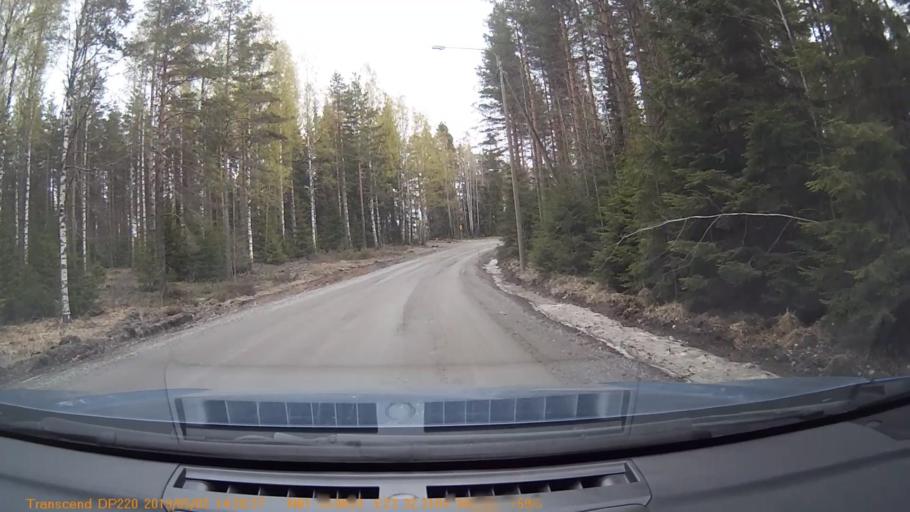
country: FI
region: Pirkanmaa
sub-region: Tampere
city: Yloejaervi
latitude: 61.5511
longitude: 23.5383
